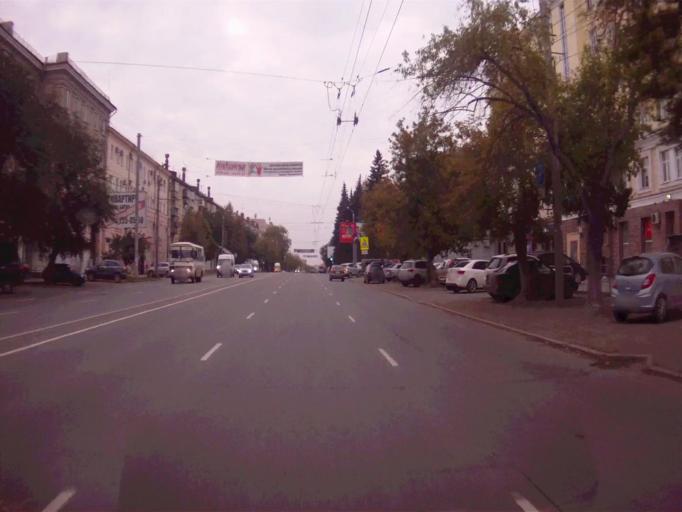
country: RU
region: Chelyabinsk
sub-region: Gorod Chelyabinsk
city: Chelyabinsk
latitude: 55.1575
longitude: 61.4129
